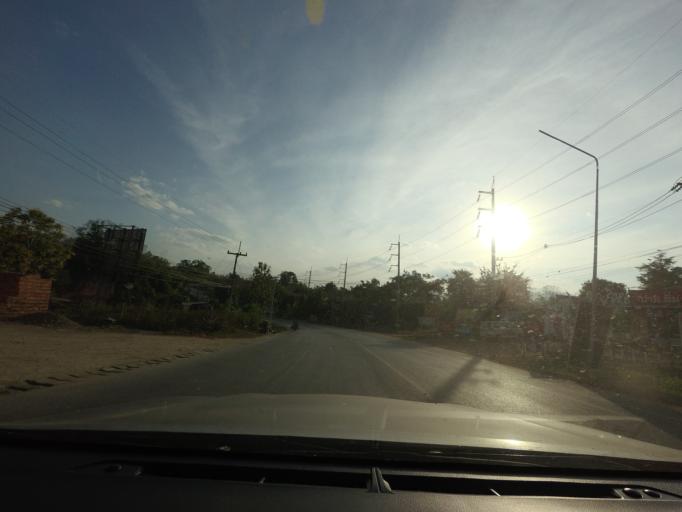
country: TH
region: Chiang Mai
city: Pai
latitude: 19.3456
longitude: 98.4330
